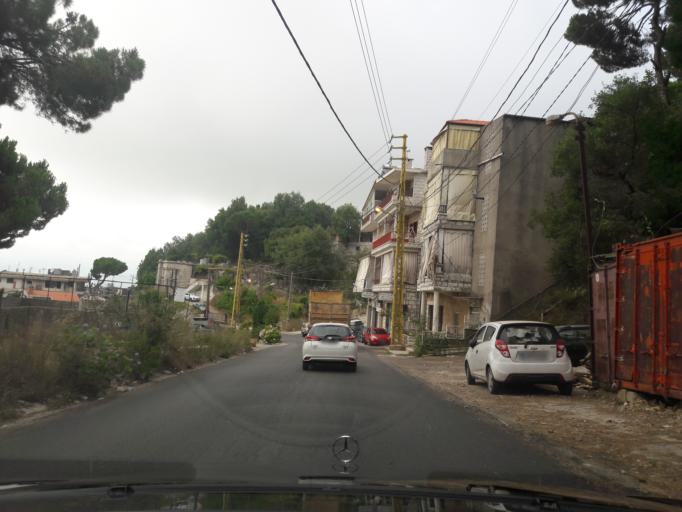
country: LB
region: Mont-Liban
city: Djounie
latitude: 33.9292
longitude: 35.7246
